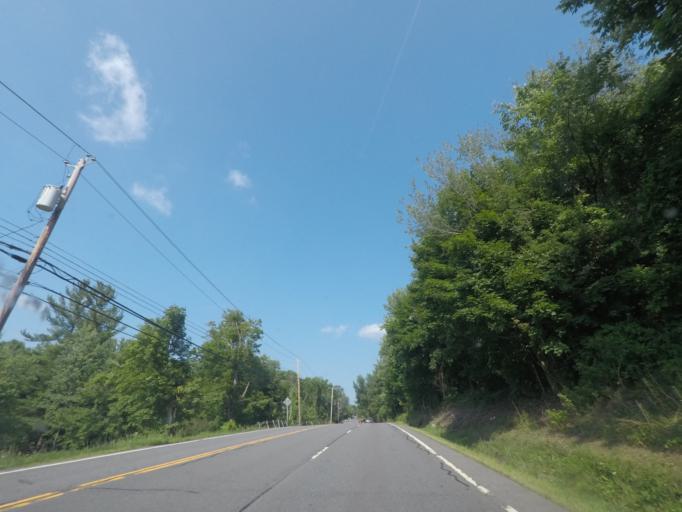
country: US
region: New York
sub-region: Rensselaer County
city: Nassau
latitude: 42.5150
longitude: -73.5961
